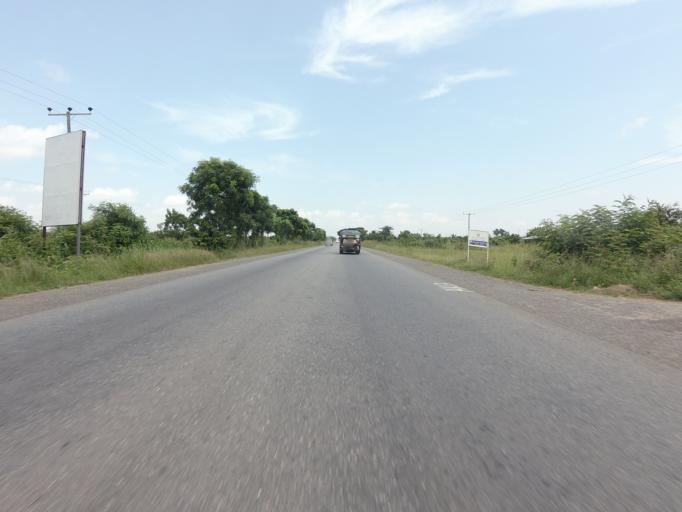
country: GH
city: Akropong
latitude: 6.0631
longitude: 0.0422
